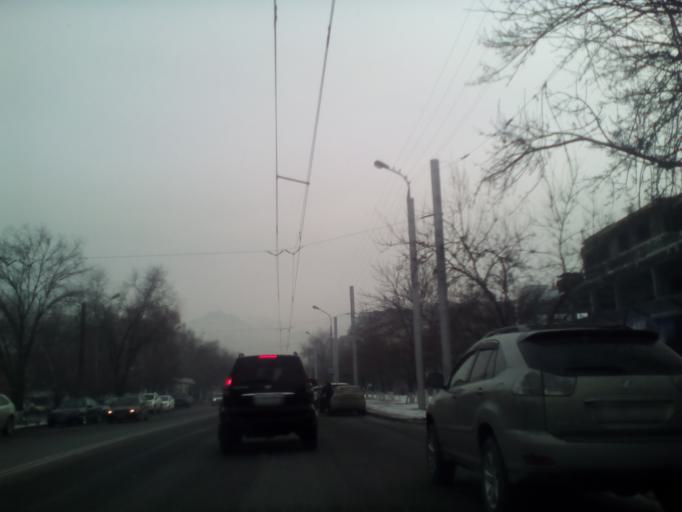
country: KZ
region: Almaty Qalasy
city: Almaty
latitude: 43.2320
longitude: 76.8326
